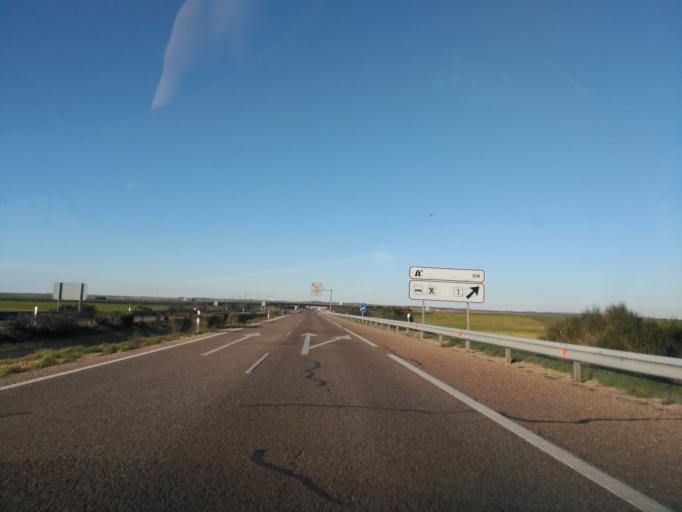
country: ES
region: Castille and Leon
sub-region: Provincia de Salamanca
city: Pajares de la Laguna
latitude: 41.0867
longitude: -5.5039
